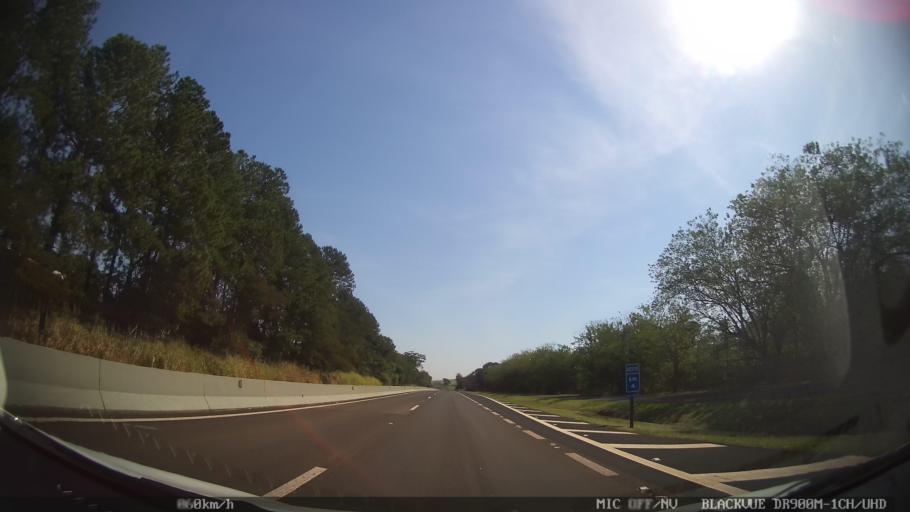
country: BR
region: Sao Paulo
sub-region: Ribeirao Preto
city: Ribeirao Preto
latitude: -21.1716
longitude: -47.8621
